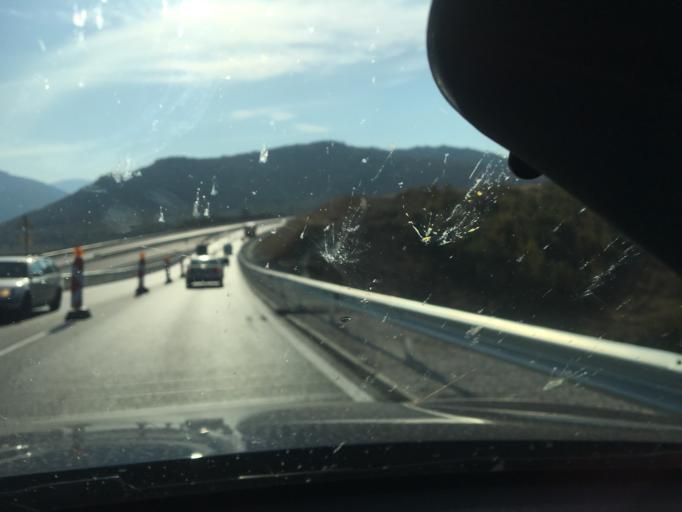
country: BG
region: Lovech
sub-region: Obshtina Yablanitsa
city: Yablanitsa
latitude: 43.0552
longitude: 24.2215
